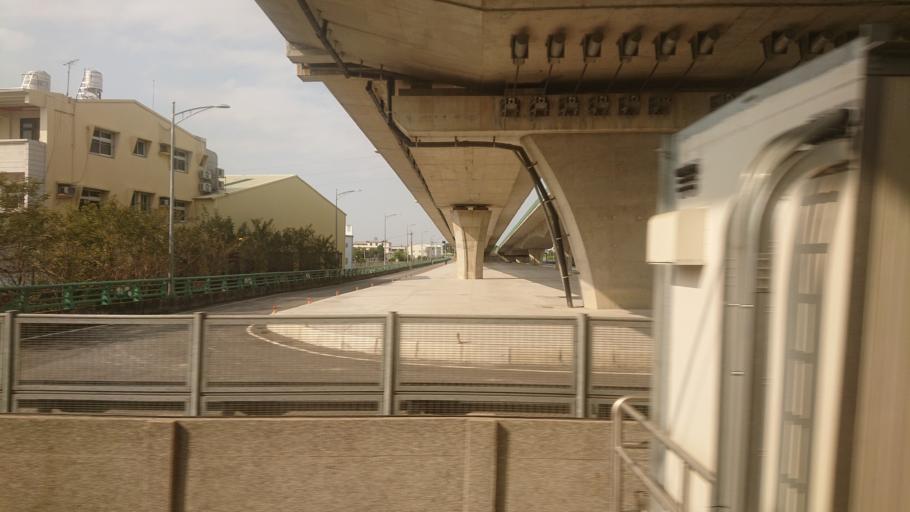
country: TW
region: Taiwan
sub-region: Nantou
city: Nantou
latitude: 23.9237
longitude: 120.5730
